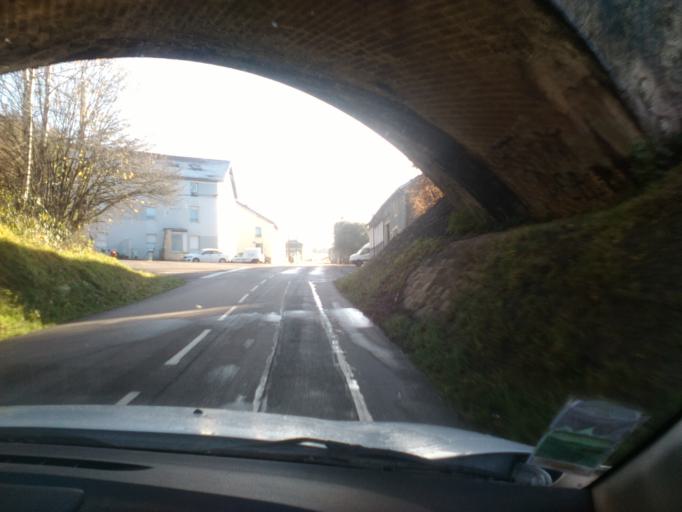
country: FR
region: Lorraine
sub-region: Departement des Vosges
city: Xertigny
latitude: 48.0513
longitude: 6.3767
